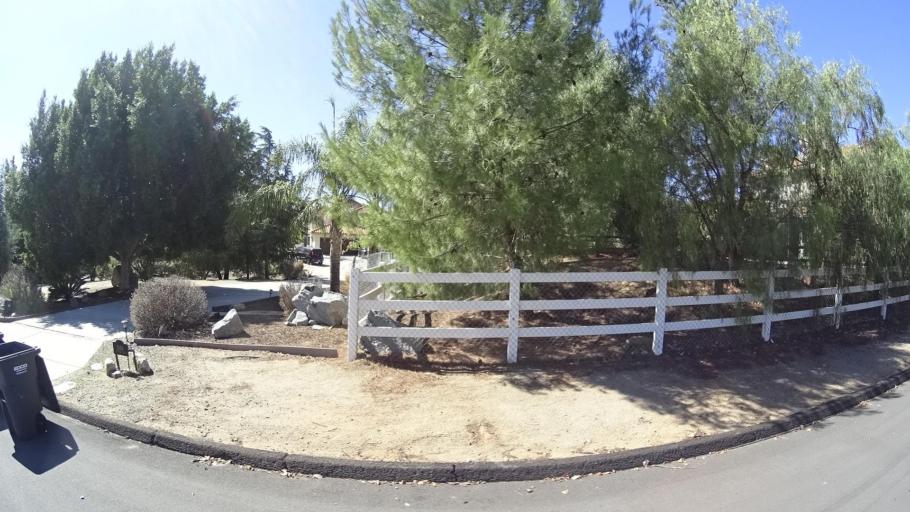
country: US
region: California
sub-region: San Diego County
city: Alpine
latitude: 32.8435
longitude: -116.7625
